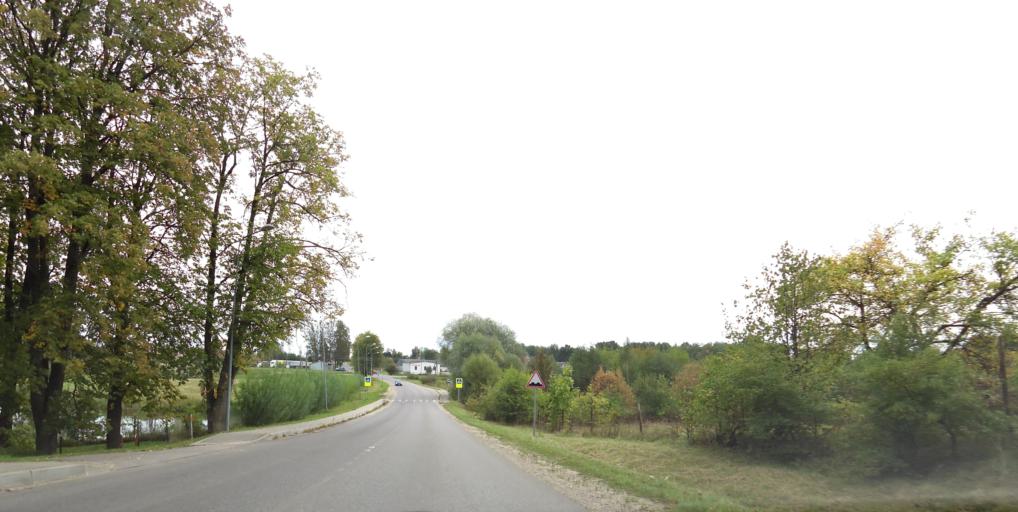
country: LT
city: Grigiskes
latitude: 54.7637
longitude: 25.0418
